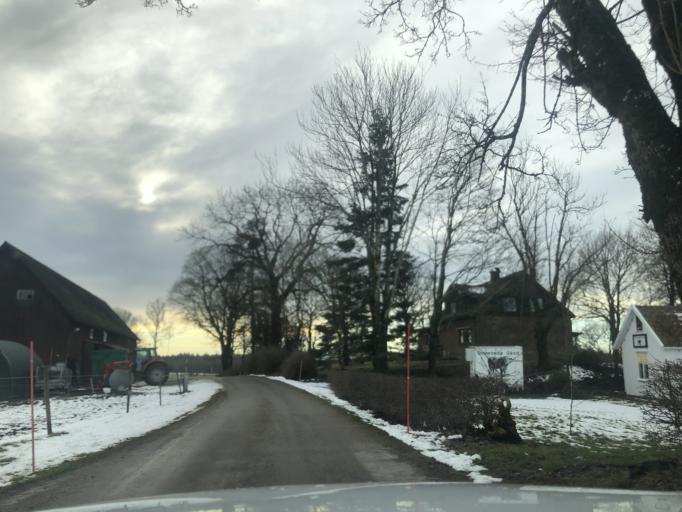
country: SE
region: Vaestra Goetaland
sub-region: Ulricehamns Kommun
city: Ulricehamn
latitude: 57.8059
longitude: 13.5091
